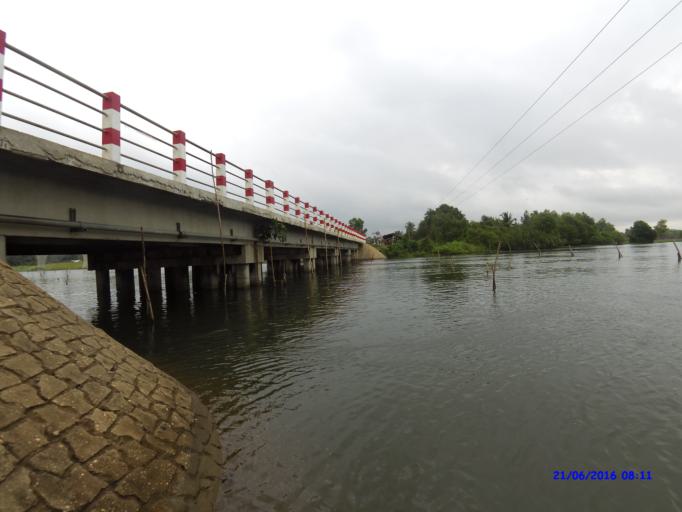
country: BJ
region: Mono
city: Come
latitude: 6.3886
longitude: 1.9426
